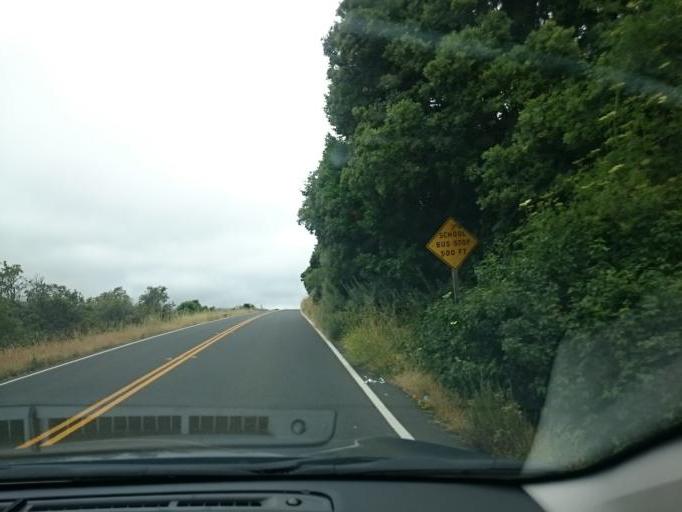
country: US
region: California
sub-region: Marin County
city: Inverness
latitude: 38.0975
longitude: -122.8305
